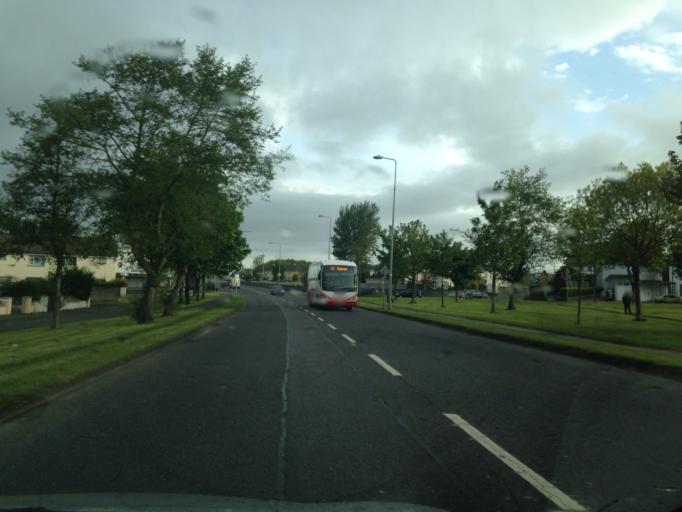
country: IE
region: Connaught
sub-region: County Galway
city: Gaillimh
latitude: 53.2844
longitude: -9.0108
